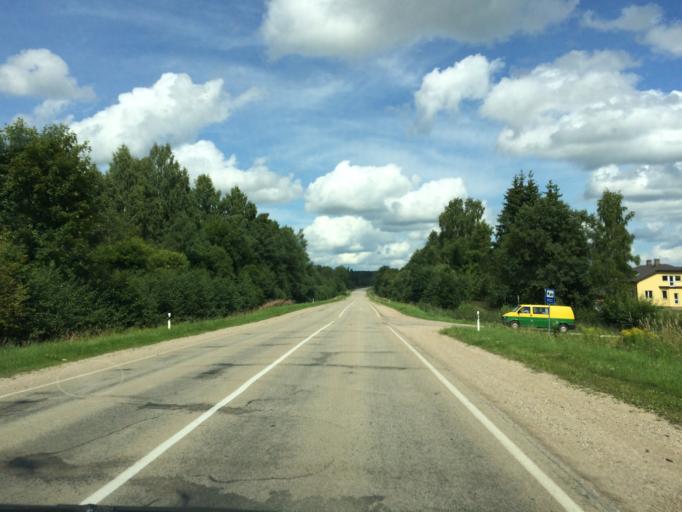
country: LV
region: Rezekne
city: Rezekne
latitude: 56.5621
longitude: 27.3649
